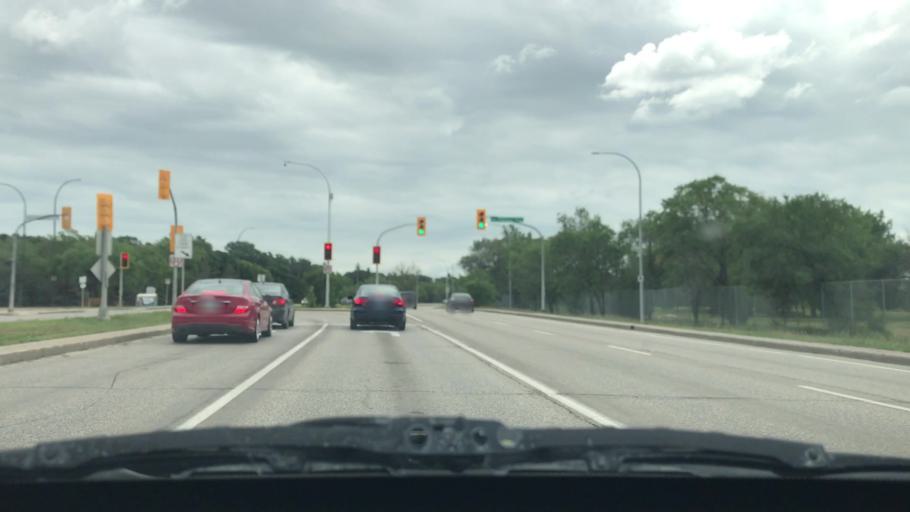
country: CA
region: Manitoba
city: Winnipeg
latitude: 49.8505
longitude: -97.1213
